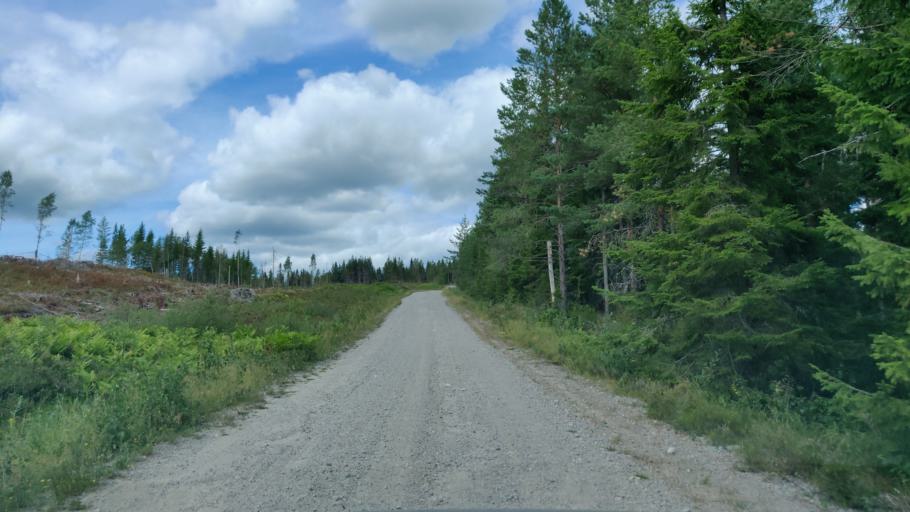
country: SE
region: Vaermland
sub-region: Hagfors Kommun
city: Hagfors
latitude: 60.0178
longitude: 13.7305
